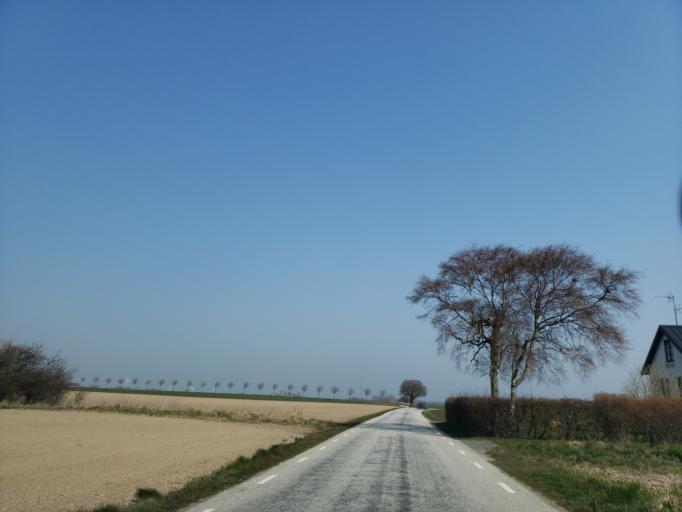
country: SE
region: Skane
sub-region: Simrishamns Kommun
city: Simrishamn
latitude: 55.5100
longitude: 14.3189
